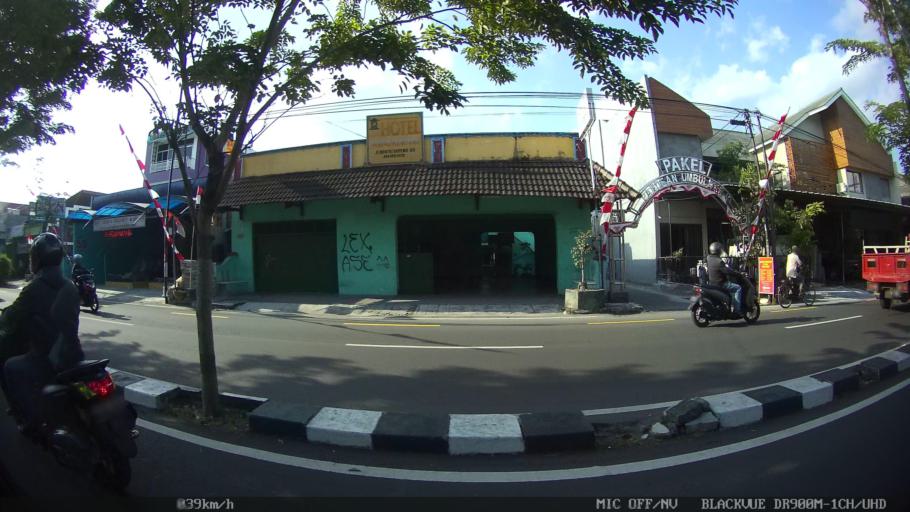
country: ID
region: Daerah Istimewa Yogyakarta
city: Yogyakarta
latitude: -7.8161
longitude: 110.3803
